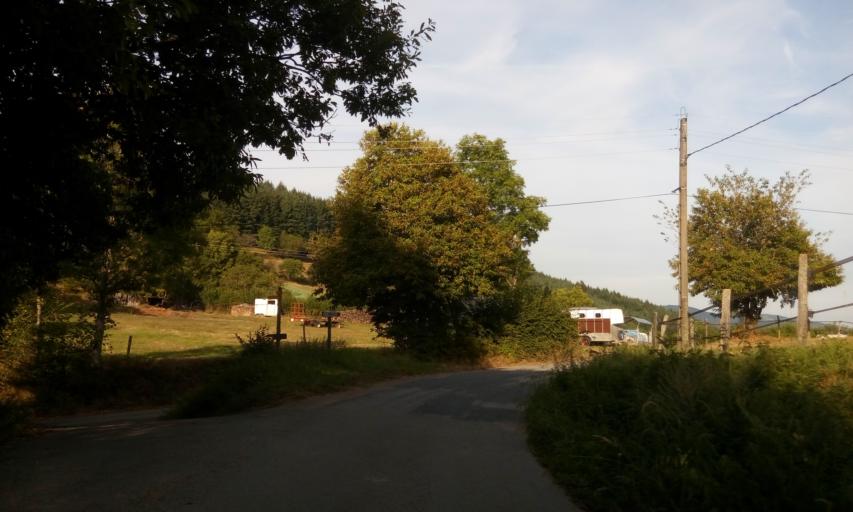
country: FR
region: Rhone-Alpes
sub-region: Departement du Rhone
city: Grandris
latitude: 45.9930
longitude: 4.4595
